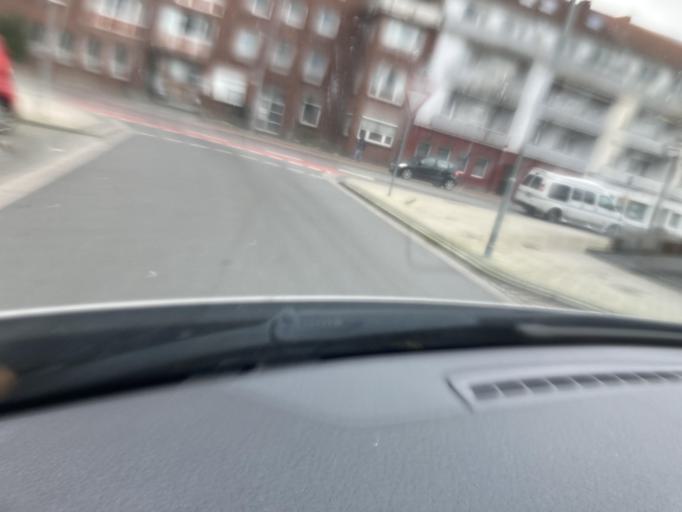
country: DE
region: Lower Saxony
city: Wilhelmshaven
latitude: 53.5258
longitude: 8.1118
